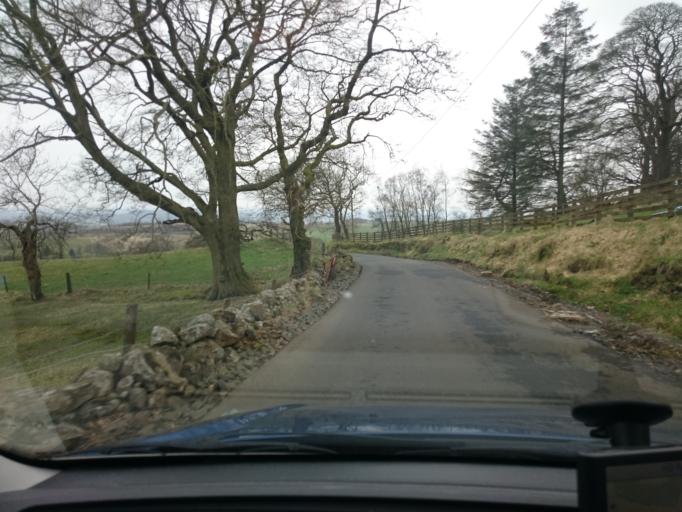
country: GB
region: Scotland
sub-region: North Lanarkshire
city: Kilsyth
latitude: 55.9942
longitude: -4.0433
